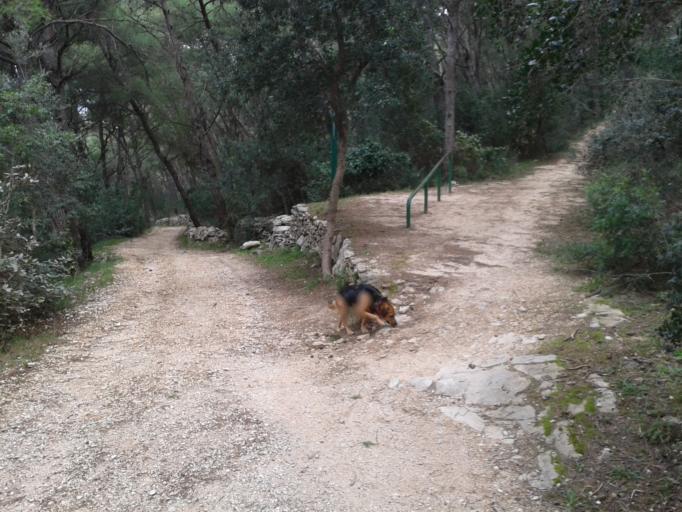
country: HR
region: Splitsko-Dalmatinska
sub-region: Grad Split
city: Split
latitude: 43.5116
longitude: 16.4029
